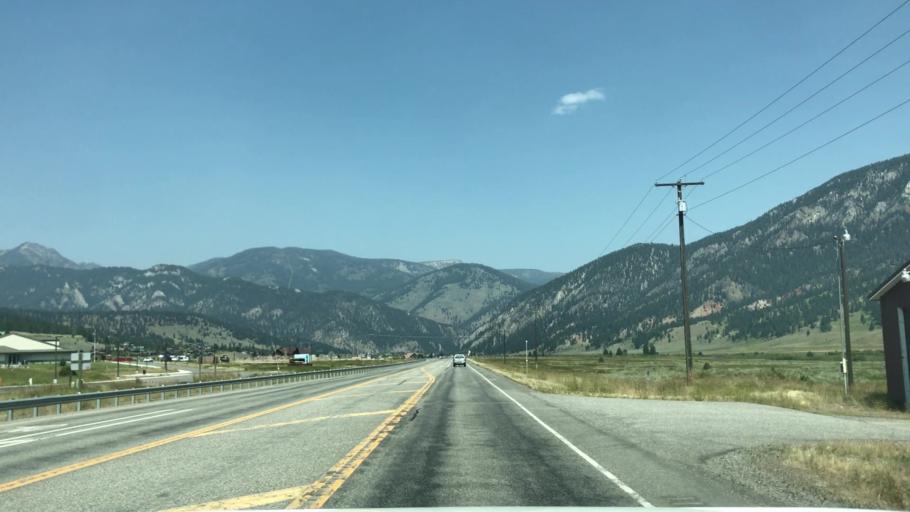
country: US
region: Montana
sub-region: Gallatin County
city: Big Sky
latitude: 45.2289
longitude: -111.2508
